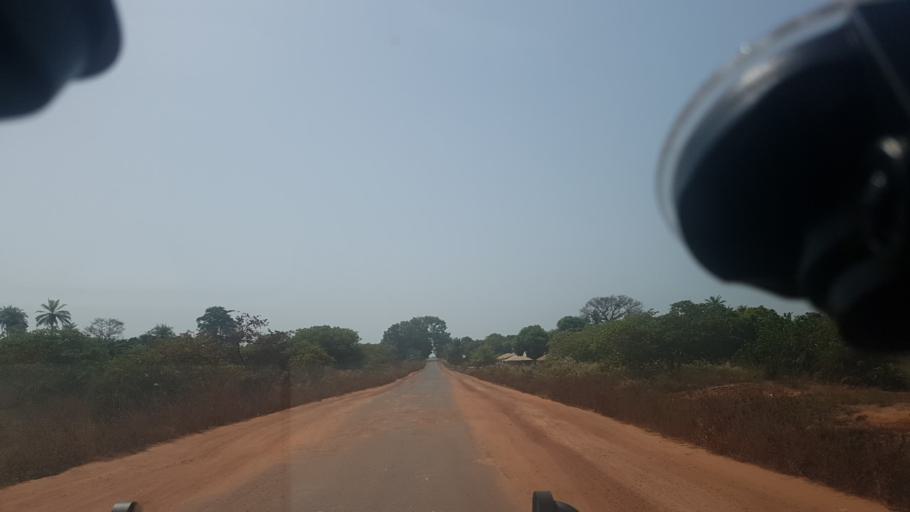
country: GW
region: Cacheu
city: Cacheu
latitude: 12.4096
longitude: -16.0592
